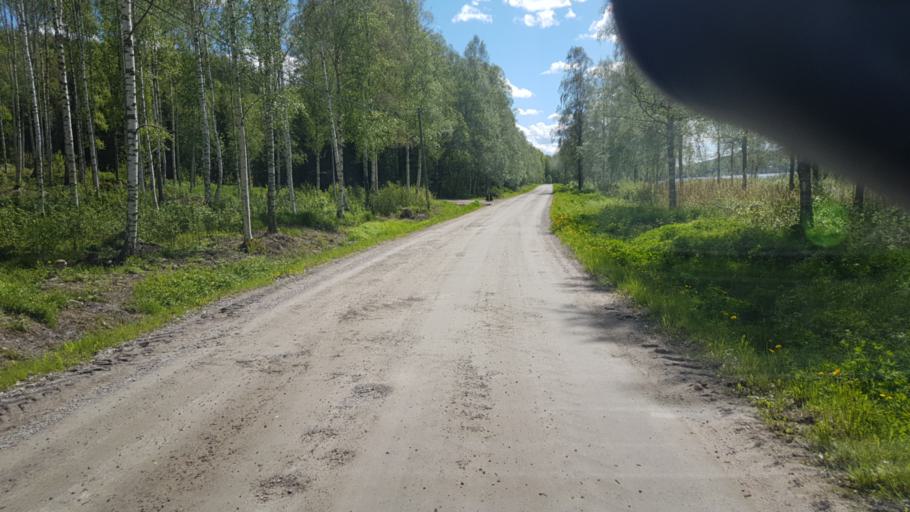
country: SE
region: Vaermland
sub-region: Arvika Kommun
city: Arvika
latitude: 59.7490
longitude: 12.8295
